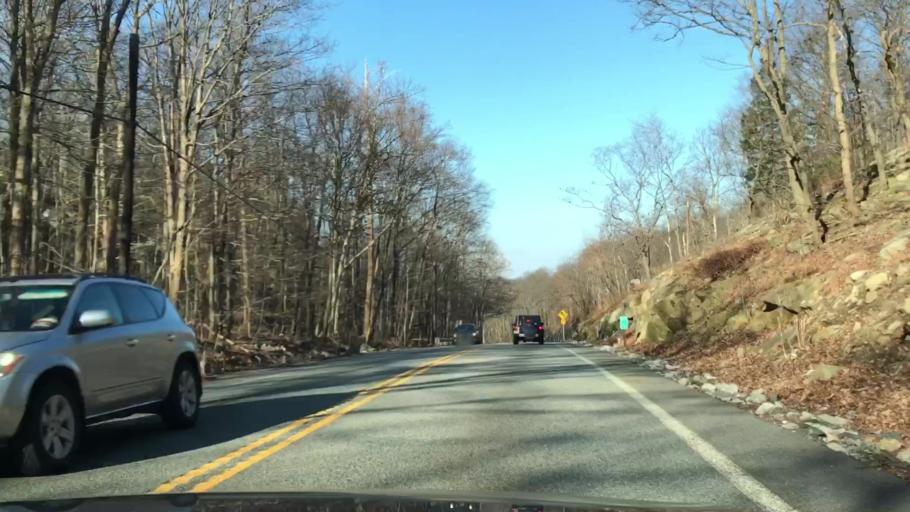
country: US
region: New Jersey
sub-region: Passaic County
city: Wanaque
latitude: 41.0619
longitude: -74.2519
